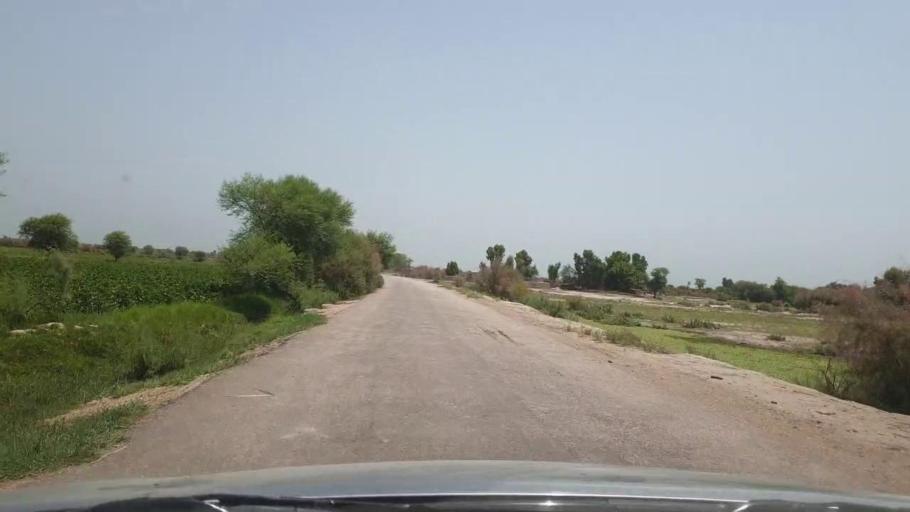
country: PK
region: Sindh
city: Pano Aqil
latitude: 27.8747
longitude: 69.1563
